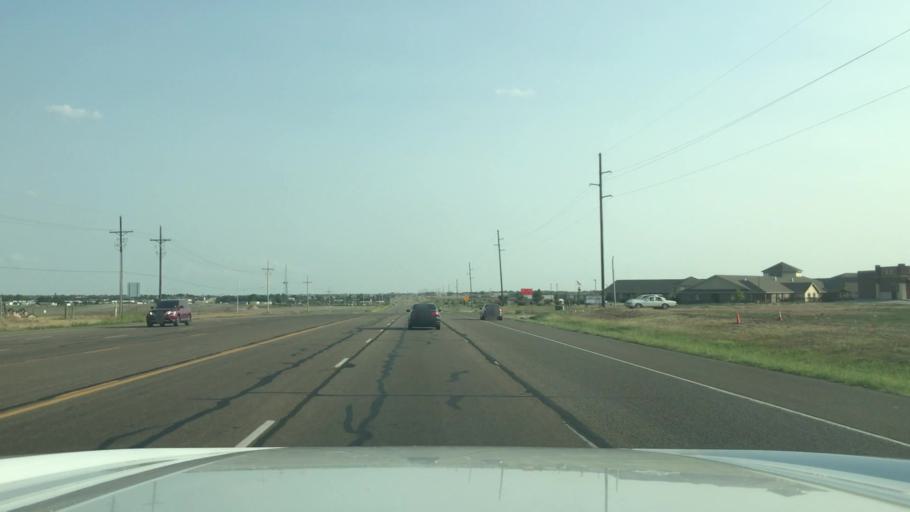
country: US
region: Texas
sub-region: Potter County
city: Amarillo
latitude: 35.1418
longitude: -101.9382
